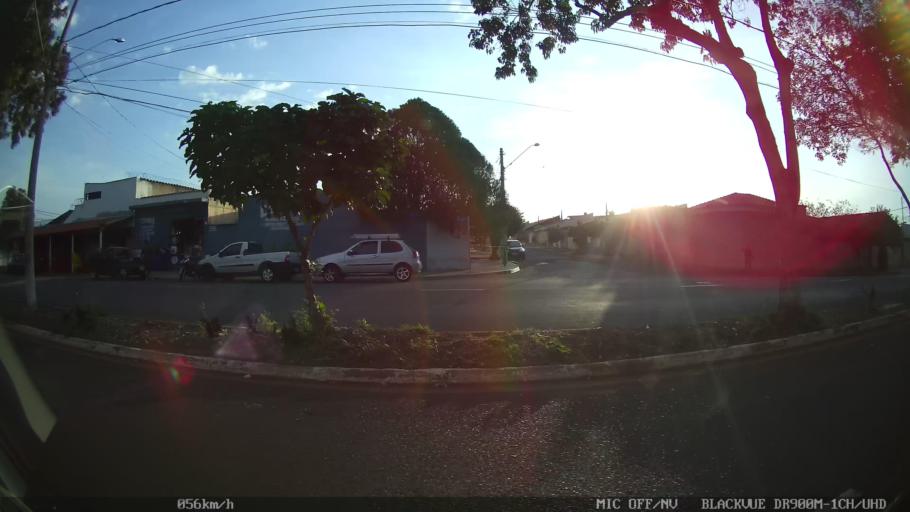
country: BR
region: Sao Paulo
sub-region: Ribeirao Preto
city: Ribeirao Preto
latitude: -21.1249
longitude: -47.8034
